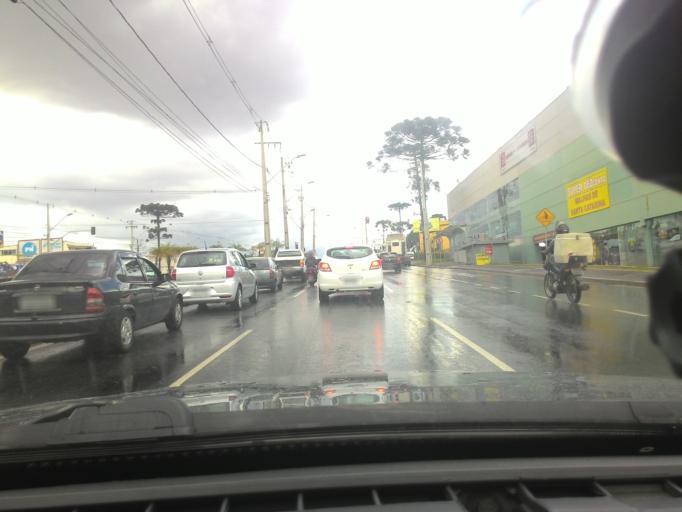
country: BR
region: Parana
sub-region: Sao Jose Dos Pinhais
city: Sao Jose dos Pinhais
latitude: -25.4921
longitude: -49.2144
